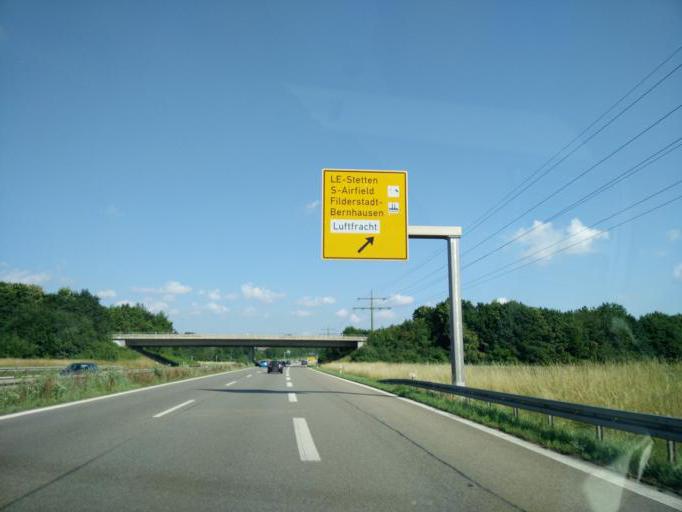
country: DE
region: Baden-Wuerttemberg
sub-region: Regierungsbezirk Stuttgart
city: Leinfelden-Echterdingen
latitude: 48.6733
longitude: 9.1879
